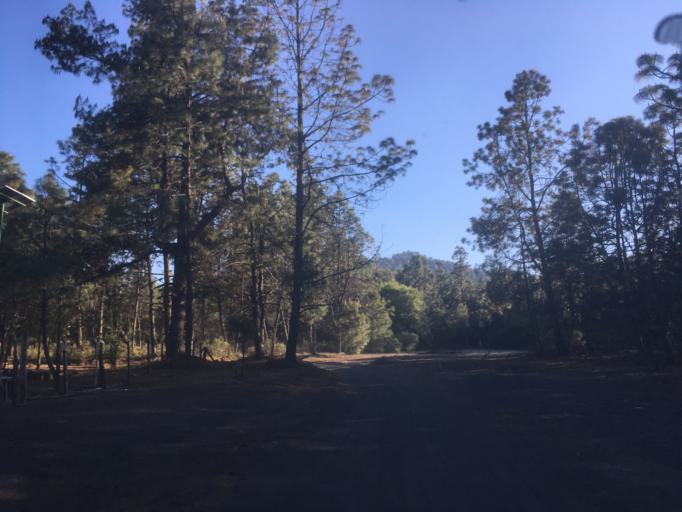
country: MX
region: Michoacan
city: Angahuan
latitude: 19.4626
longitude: -102.2390
